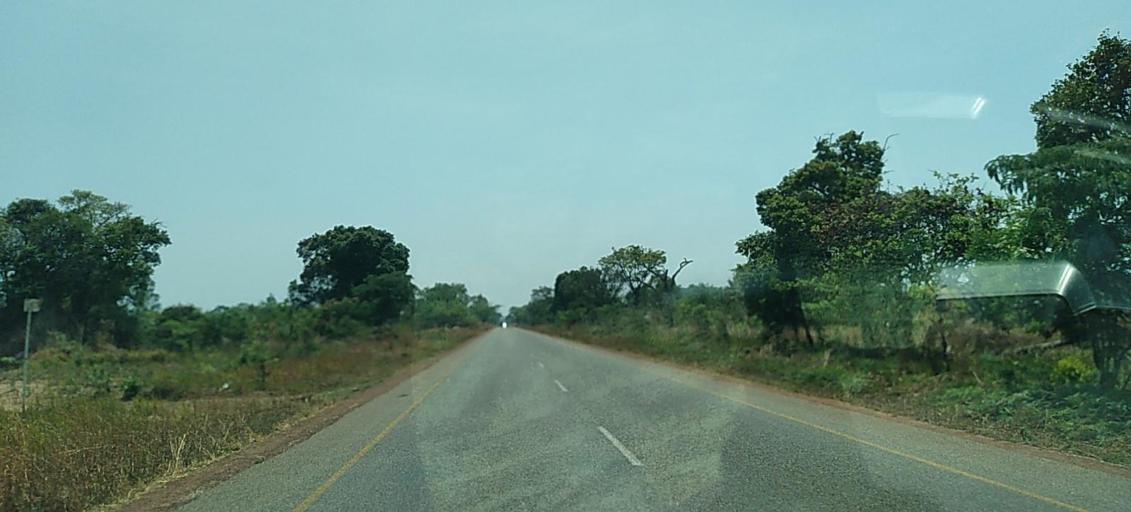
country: ZM
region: North-Western
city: Solwezi
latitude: -12.3963
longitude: 26.1576
